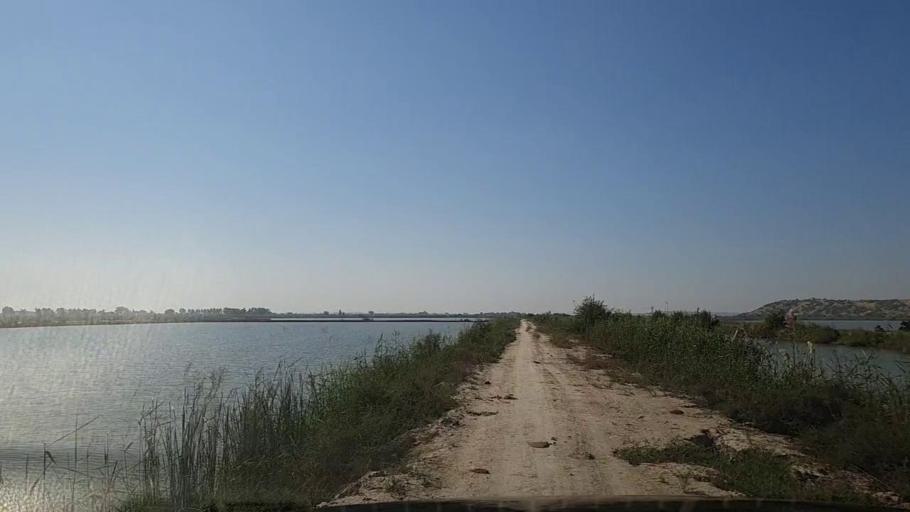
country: PK
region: Sindh
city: Thatta
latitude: 24.6801
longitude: 67.8904
